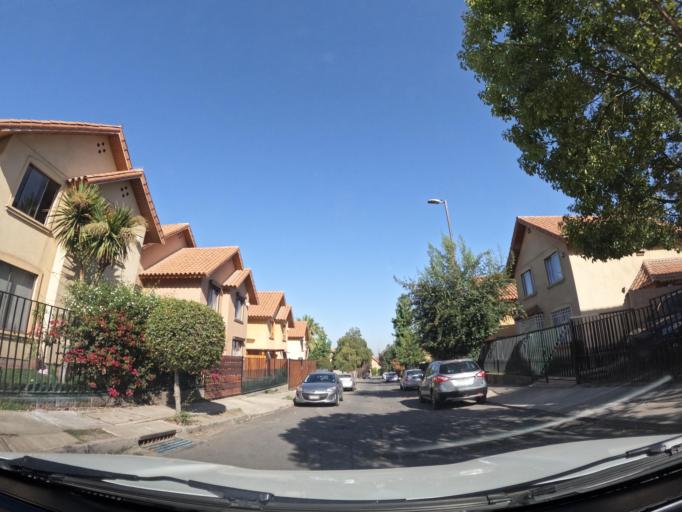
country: CL
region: Santiago Metropolitan
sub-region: Provincia de Santiago
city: Villa Presidente Frei, Nunoa, Santiago, Chile
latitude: -33.5096
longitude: -70.5456
